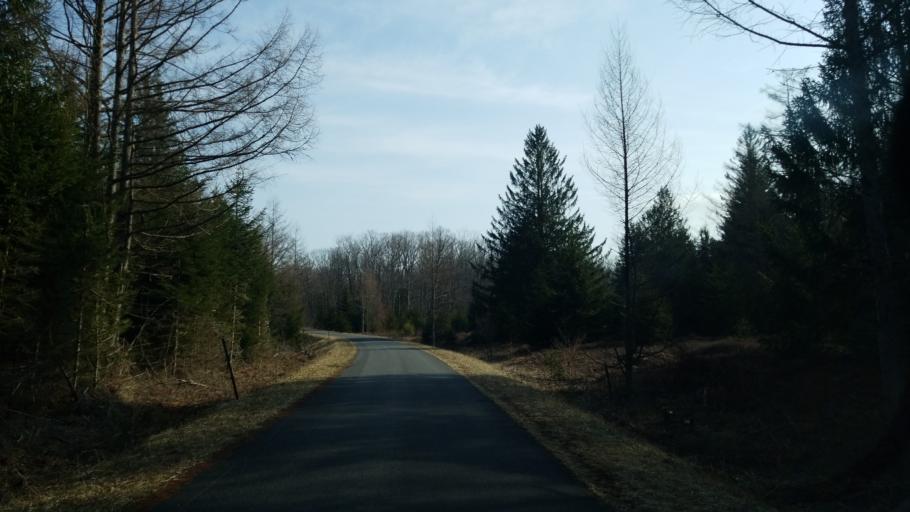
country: US
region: Pennsylvania
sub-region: Clearfield County
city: Shiloh
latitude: 41.2295
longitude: -78.2121
